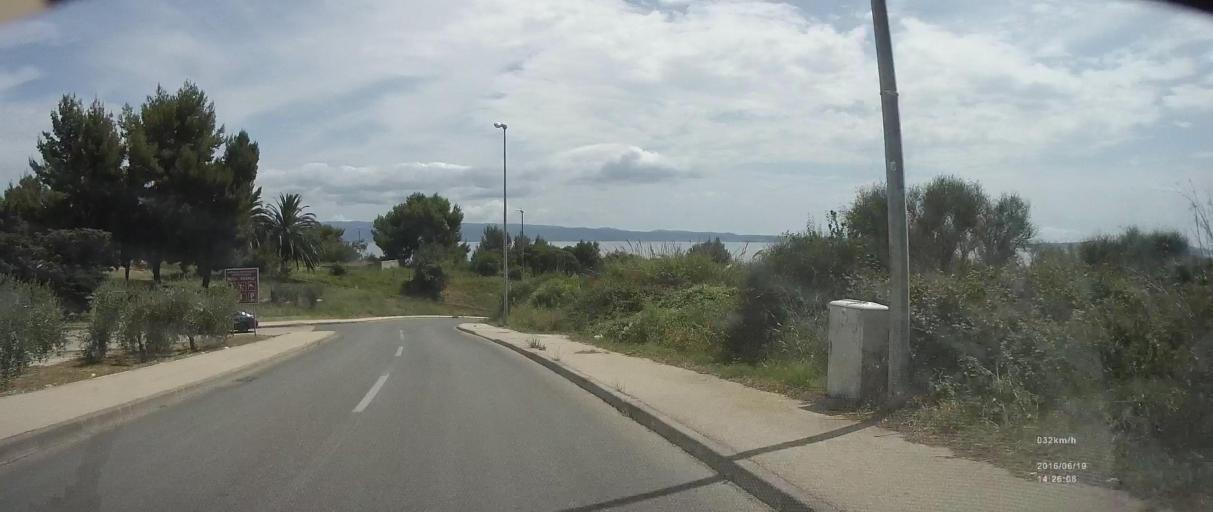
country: HR
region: Splitsko-Dalmatinska
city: Kamen
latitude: 43.5029
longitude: 16.4924
